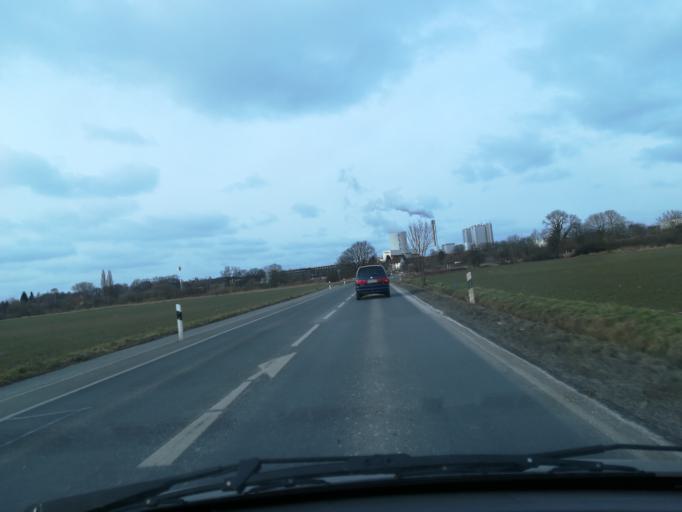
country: DE
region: Lower Saxony
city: Auf der Horst
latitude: 52.4102
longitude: 9.6464
